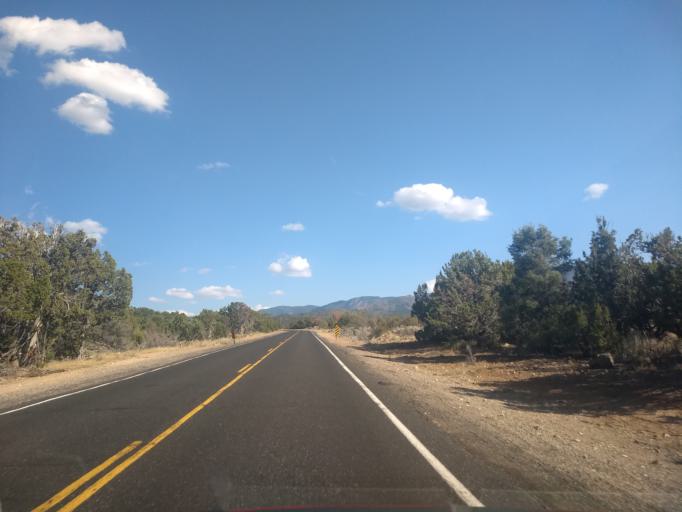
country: US
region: Utah
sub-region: Washington County
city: Enterprise
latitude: 37.4179
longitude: -113.5709
